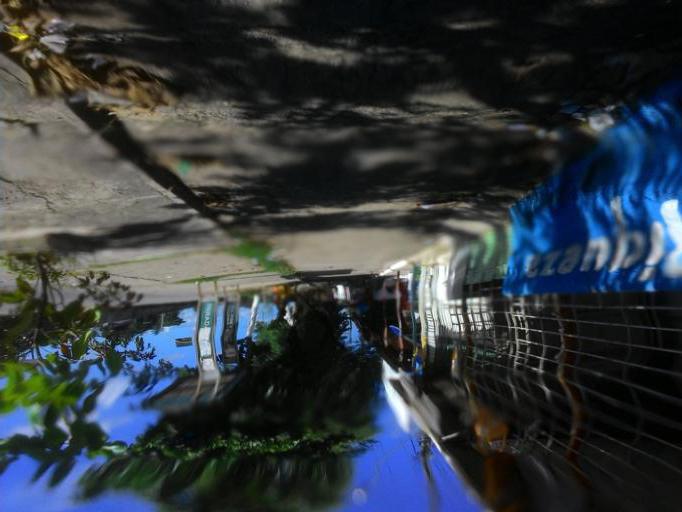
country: BR
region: Pernambuco
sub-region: Olinda
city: Olinda
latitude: -7.9944
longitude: -34.8547
